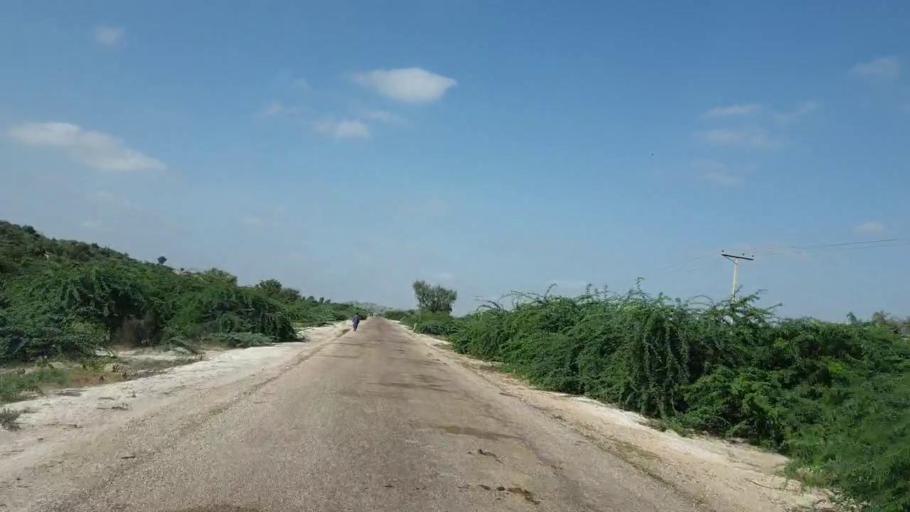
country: PK
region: Sindh
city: Mithi
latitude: 24.5300
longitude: 69.8365
